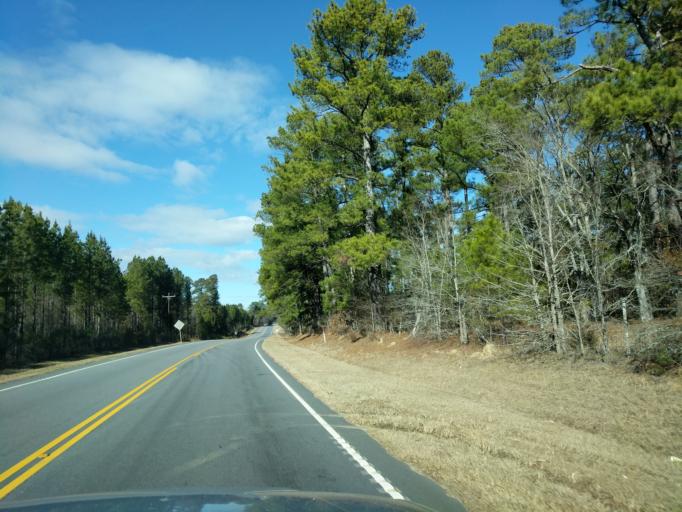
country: US
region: South Carolina
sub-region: Edgefield County
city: Edgefield
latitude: 33.9265
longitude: -82.0459
